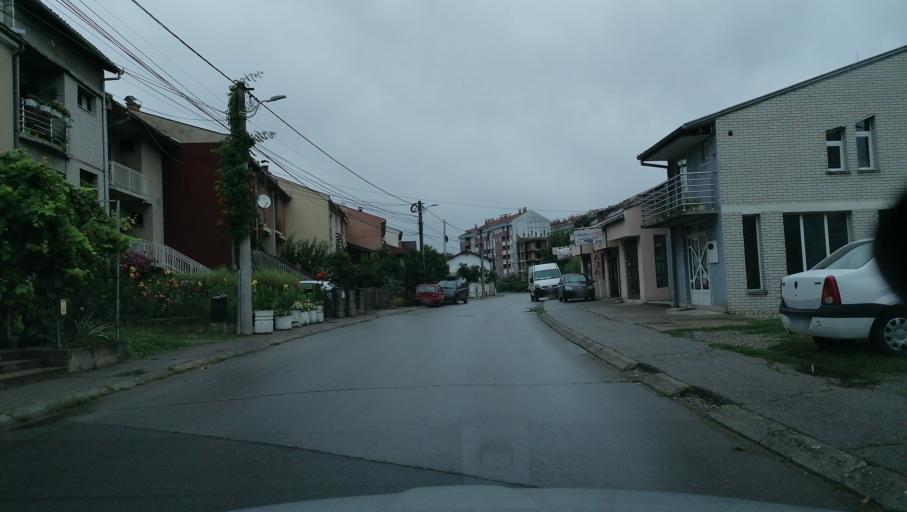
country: RS
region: Central Serbia
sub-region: Rasinski Okrug
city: Krusevac
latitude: 43.5676
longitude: 21.3284
